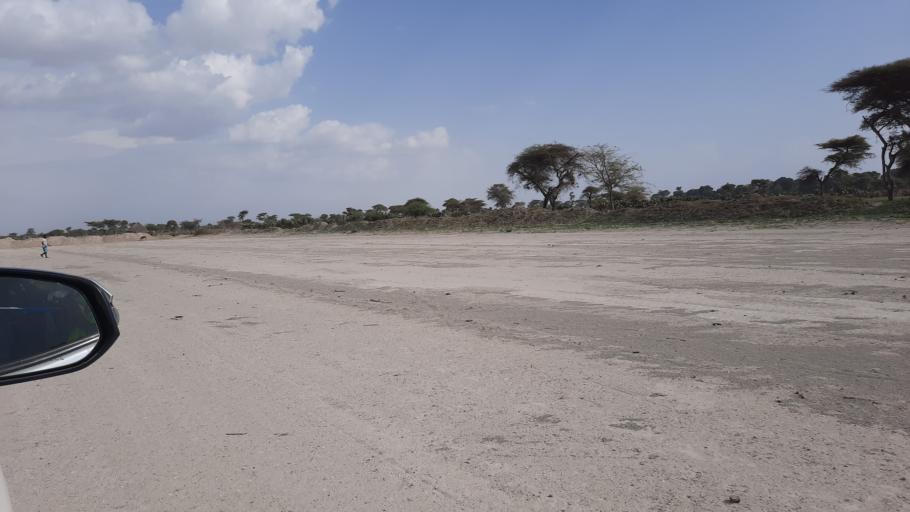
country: ET
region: Oromiya
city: Ziway
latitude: 7.7032
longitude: 38.6400
